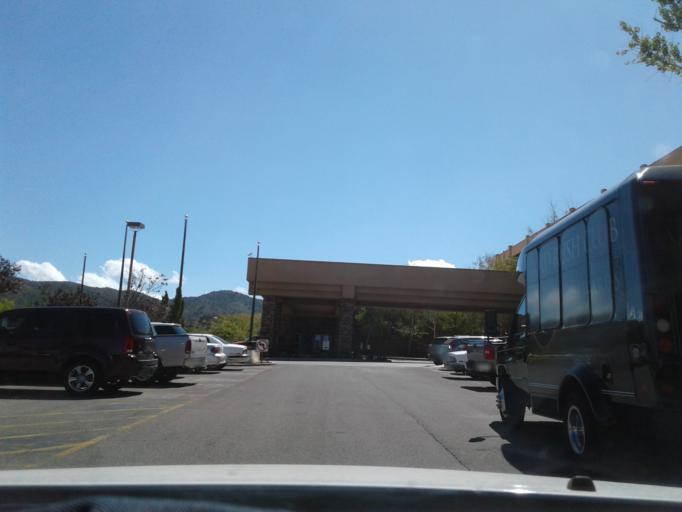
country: US
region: Arizona
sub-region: Yavapai County
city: Prescott
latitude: 34.5516
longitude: -112.4470
